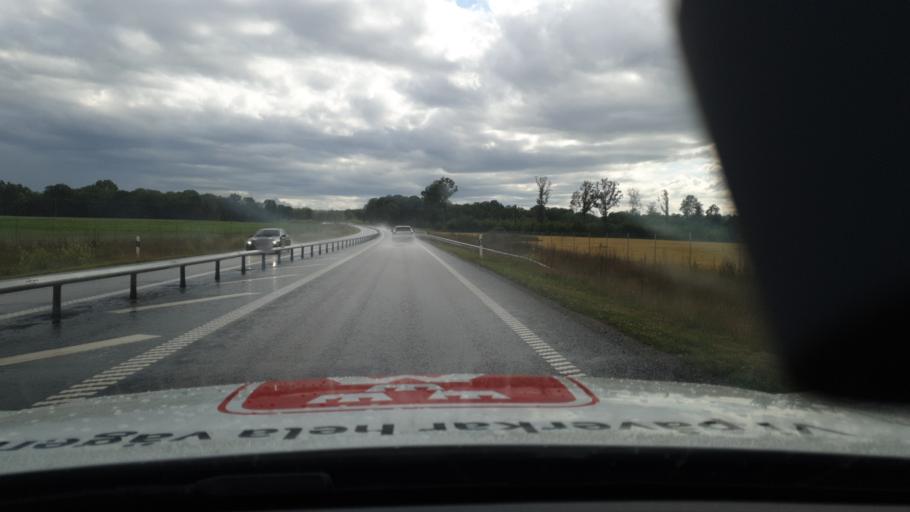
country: SE
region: Vaestra Goetaland
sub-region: Gotene Kommun
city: Kallby
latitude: 58.4899
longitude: 13.2850
